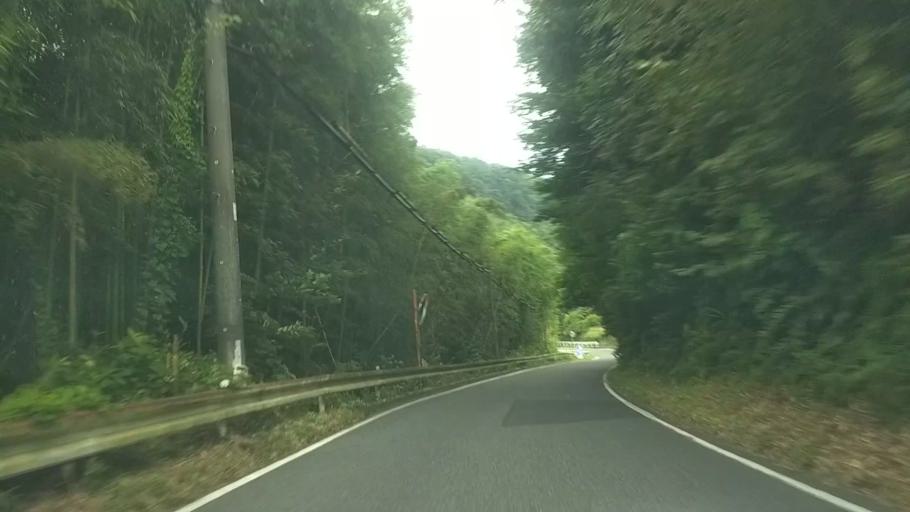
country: JP
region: Chiba
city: Kimitsu
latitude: 35.2475
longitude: 139.9923
